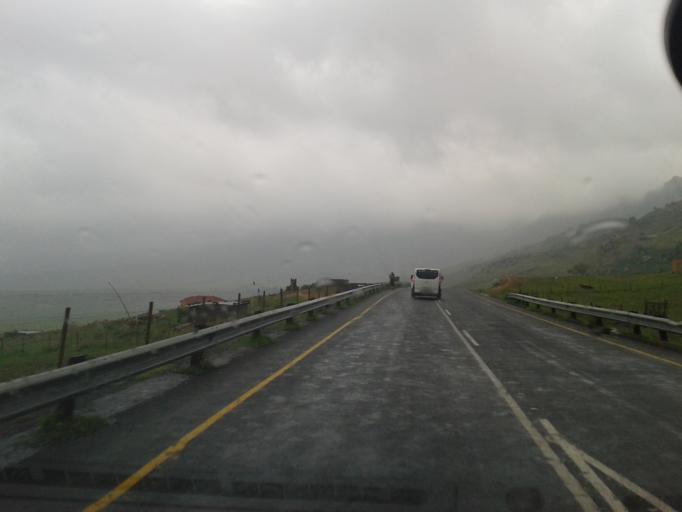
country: LS
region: Maseru
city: Maseru
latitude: -29.4293
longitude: 27.4691
